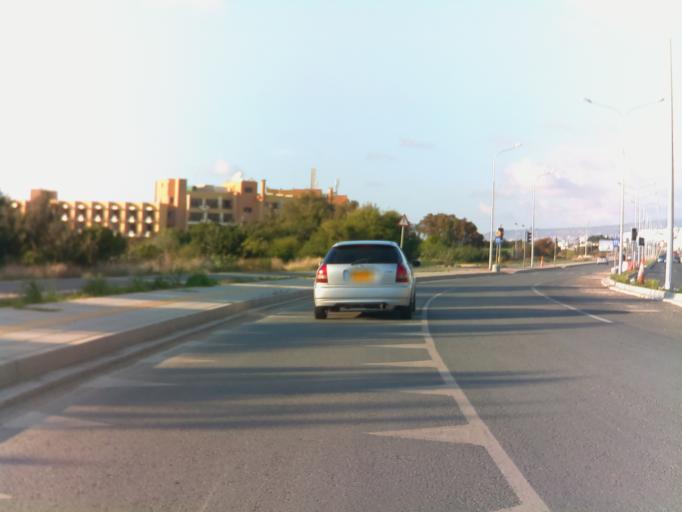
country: CY
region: Pafos
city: Paphos
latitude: 34.7775
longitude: 32.4068
